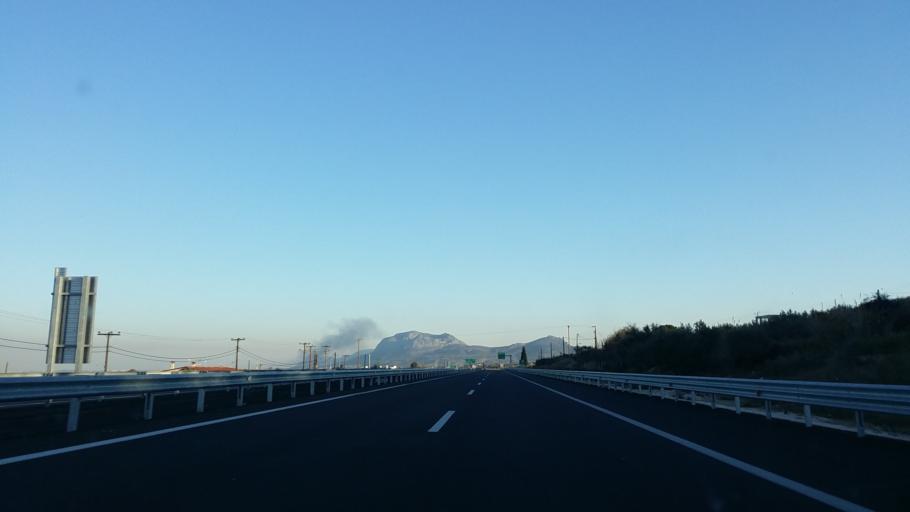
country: GR
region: Peloponnese
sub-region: Nomos Korinthias
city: Vokhaiko
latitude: 37.9370
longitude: 22.7727
